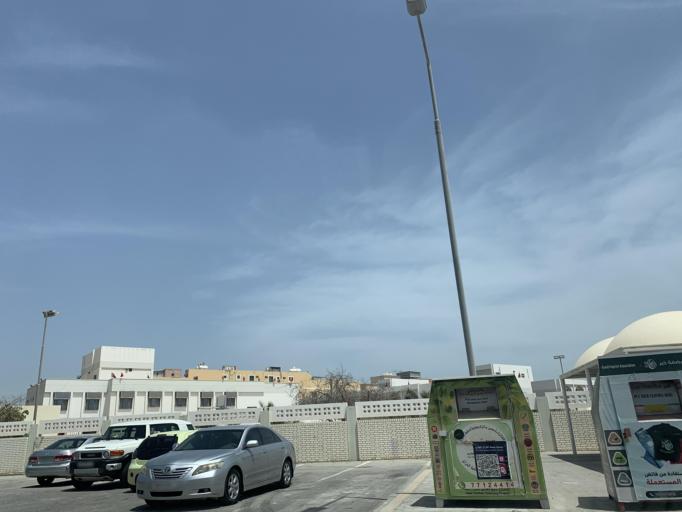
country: BH
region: Northern
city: Ar Rifa'
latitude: 26.1411
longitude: 50.5641
